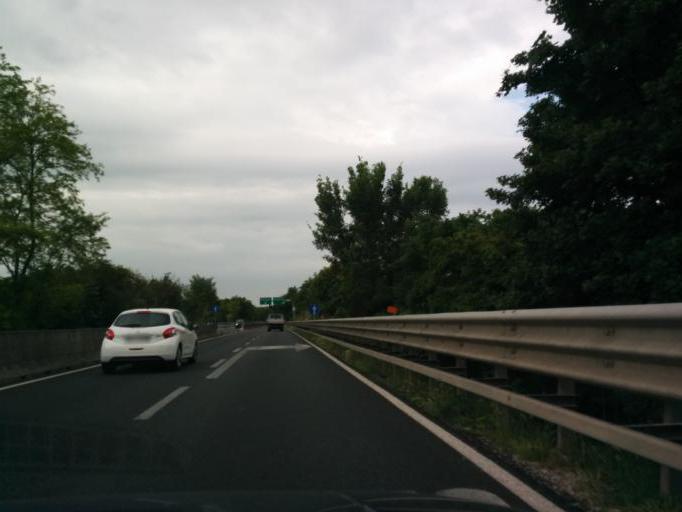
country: IT
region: Tuscany
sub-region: Province of Florence
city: San Casciano in Val di Pesa
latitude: 43.6225
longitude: 11.1850
